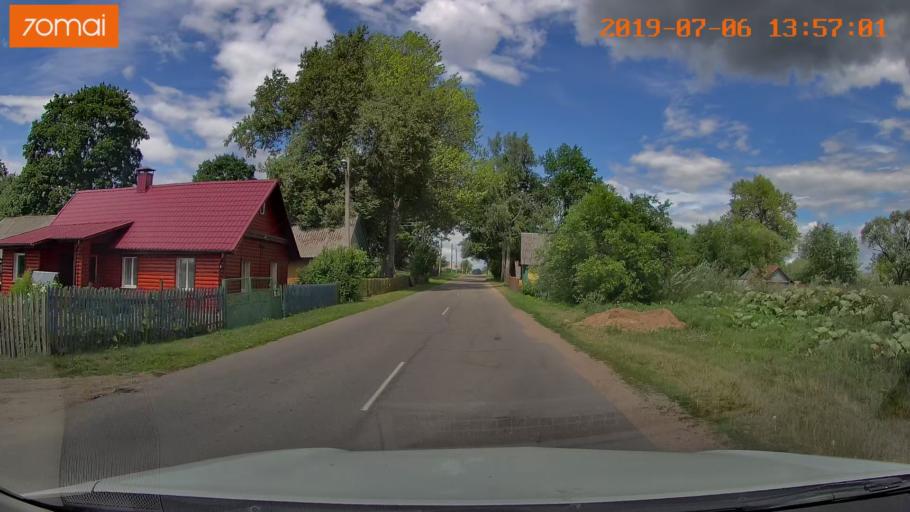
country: BY
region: Minsk
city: Ivyanyets
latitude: 53.7706
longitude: 26.8054
